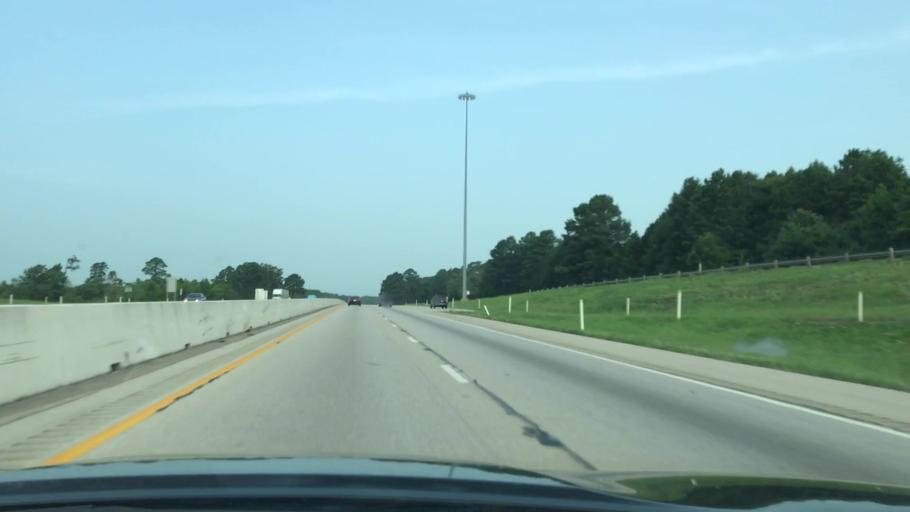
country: US
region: Texas
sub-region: Gregg County
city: Kilgore
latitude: 32.4329
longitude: -94.8638
